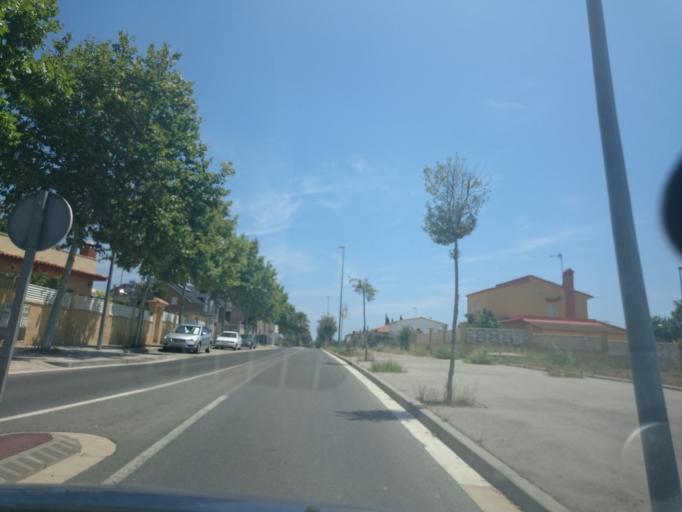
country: ES
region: Catalonia
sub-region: Provincia de Barcelona
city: Cubelles
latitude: 41.2171
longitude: 1.6914
